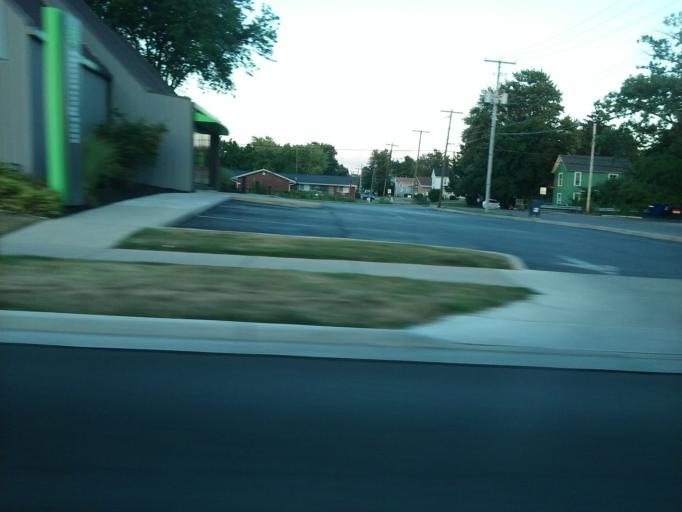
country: US
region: Ohio
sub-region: Hancock County
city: Findlay
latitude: 41.0581
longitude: -83.6500
